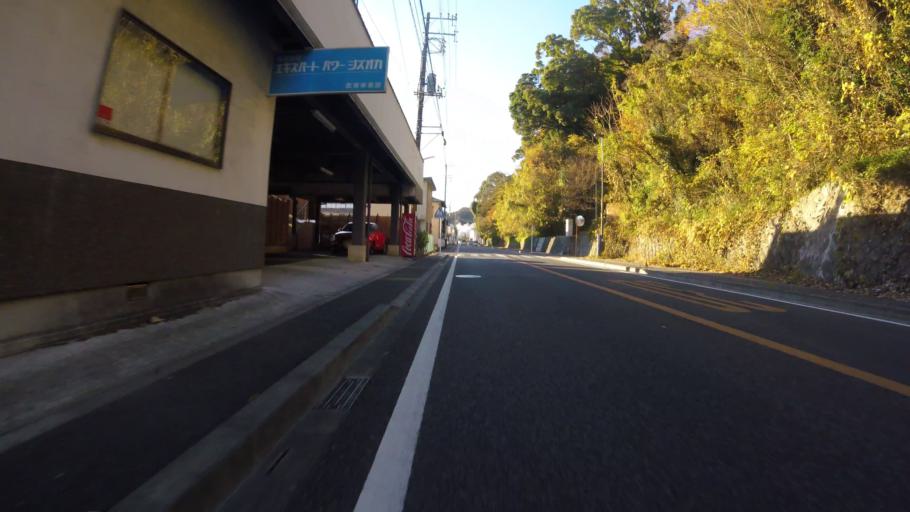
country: JP
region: Shizuoka
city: Mishima
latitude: 35.0336
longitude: 138.9371
